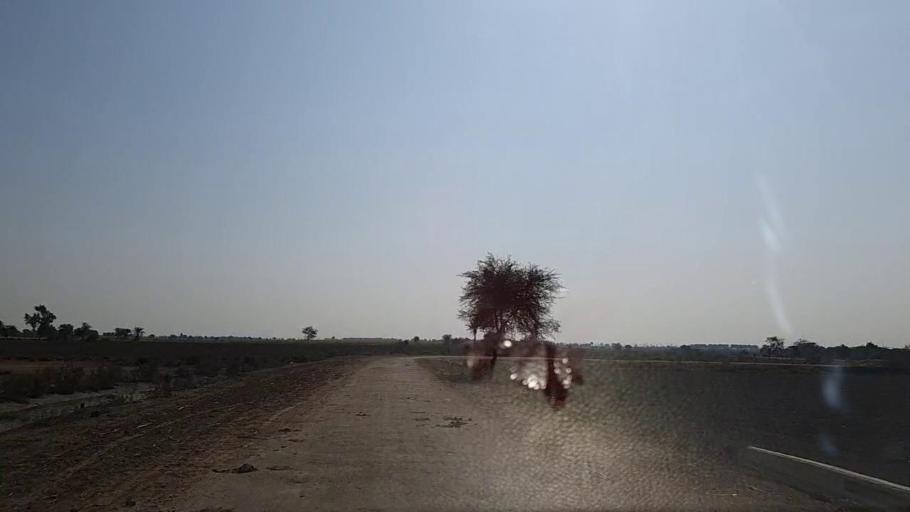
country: PK
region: Sindh
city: Sanghar
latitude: 25.9841
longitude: 69.0615
